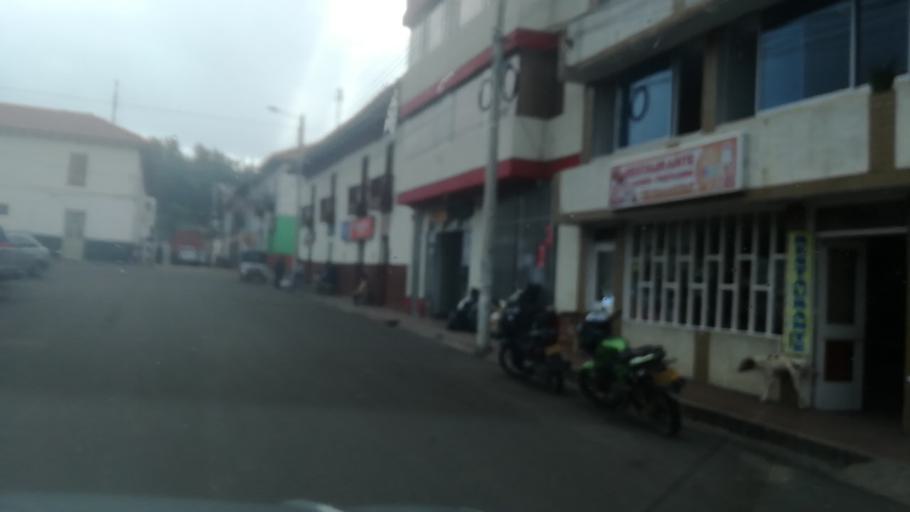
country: CO
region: Boyaca
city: Socha Viejo
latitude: 5.9979
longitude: -72.6928
